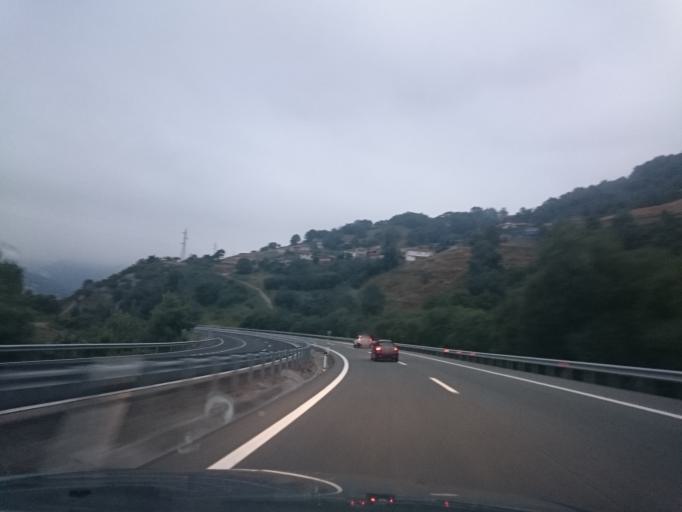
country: ES
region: Asturias
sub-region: Province of Asturias
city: Pola de Lena
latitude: 43.0635
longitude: -5.8208
